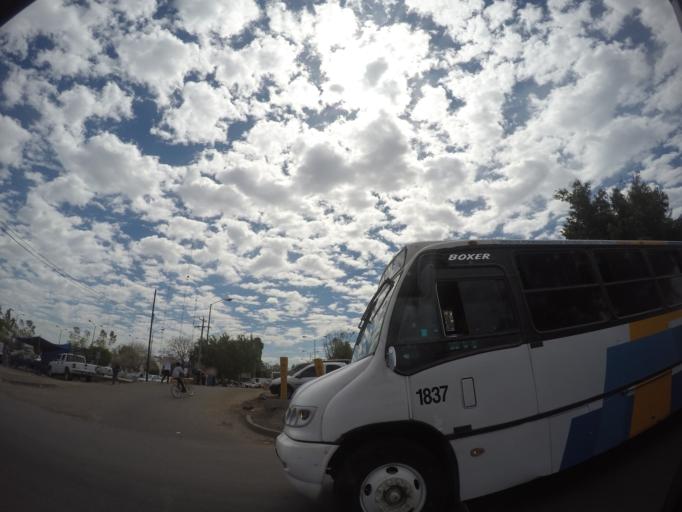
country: MX
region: Guanajuato
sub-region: Leon
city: San Antonio de los Tepetates
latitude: 21.0484
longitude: -101.6902
